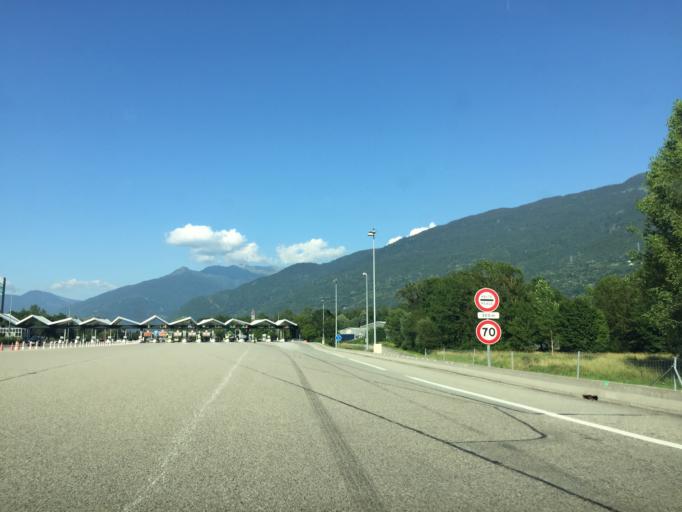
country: FR
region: Rhone-Alpes
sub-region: Departement de la Savoie
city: Sainte-Helene-sur-Isere
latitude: 45.6188
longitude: 6.3096
